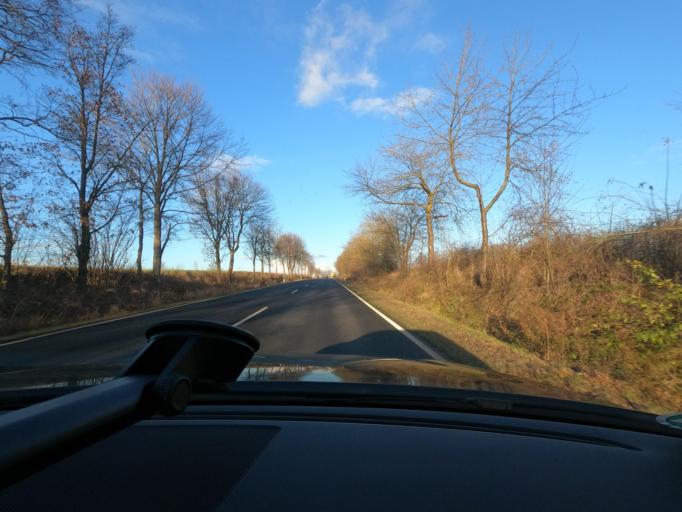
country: DE
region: Lower Saxony
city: Duderstadt
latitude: 51.5319
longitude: 10.2778
